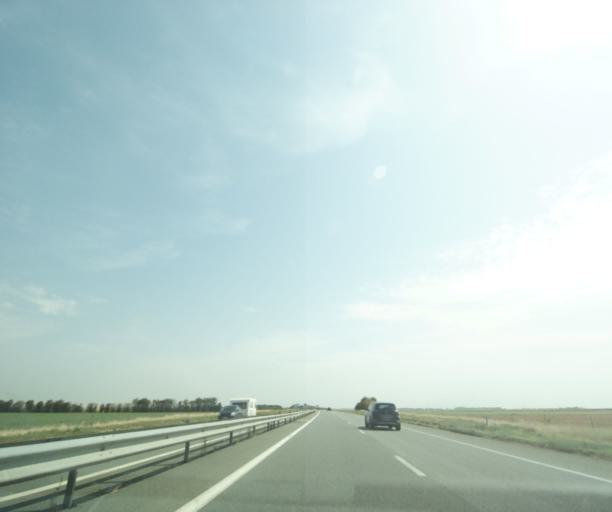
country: FR
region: Pays de la Loire
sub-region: Departement de la Vendee
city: Fontenay-le-Comte
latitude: 46.4238
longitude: -0.7838
